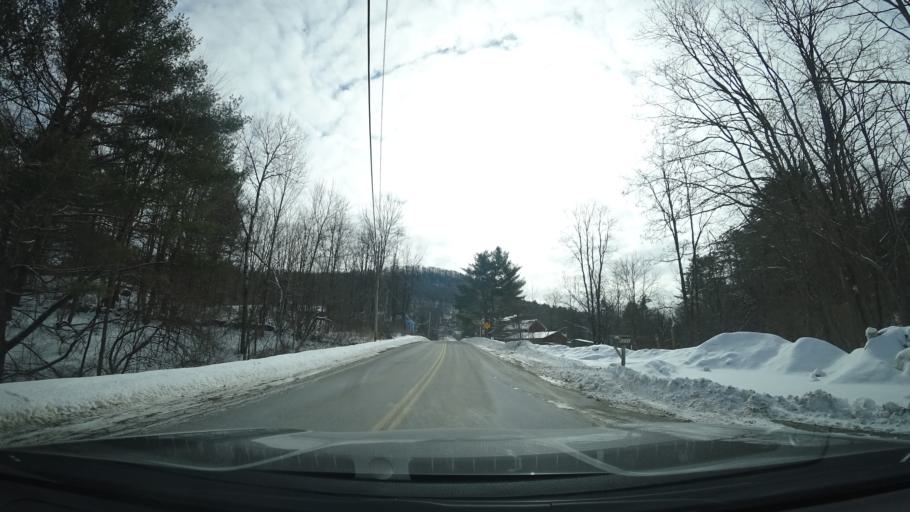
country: US
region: New York
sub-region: Washington County
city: Greenwich
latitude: 43.2396
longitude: -73.3799
